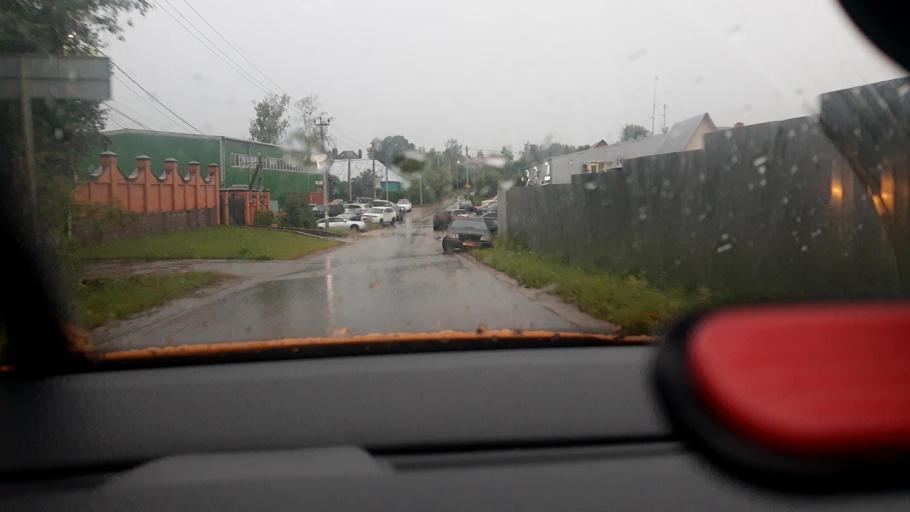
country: RU
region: Moskovskaya
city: Alabushevo
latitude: 56.0049
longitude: 37.1347
